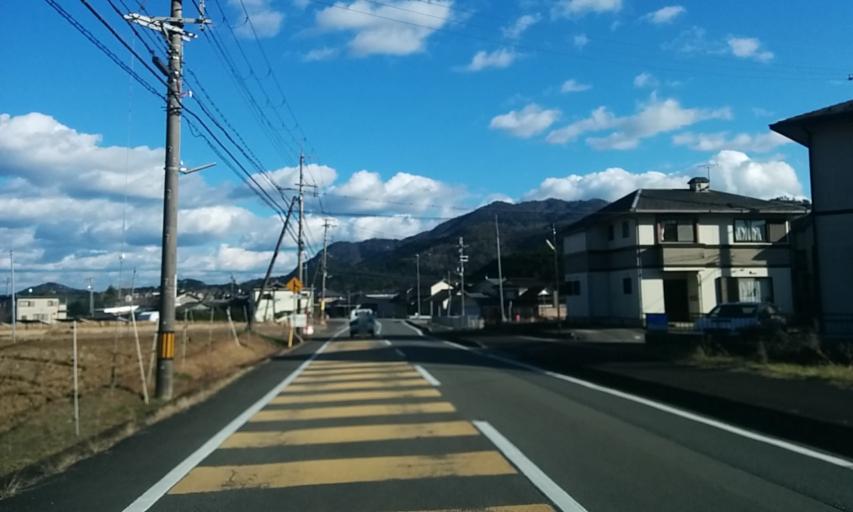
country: JP
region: Kyoto
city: Fukuchiyama
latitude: 35.2831
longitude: 135.0483
